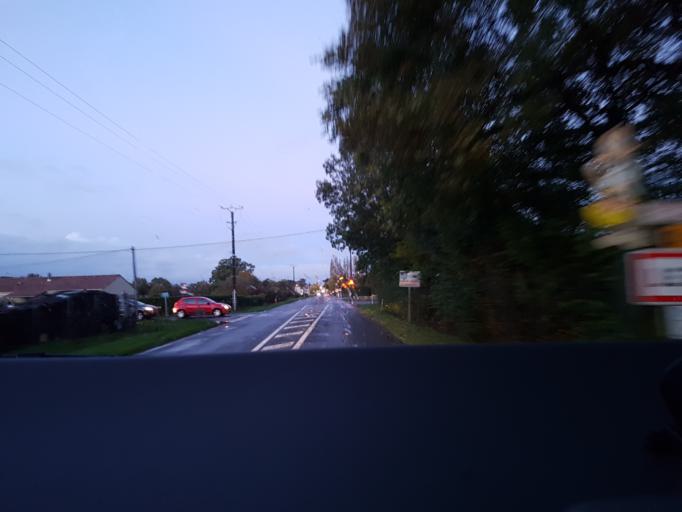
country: FR
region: Poitou-Charentes
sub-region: Departement des Deux-Sevres
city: Lezay
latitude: 46.2591
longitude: -0.0177
